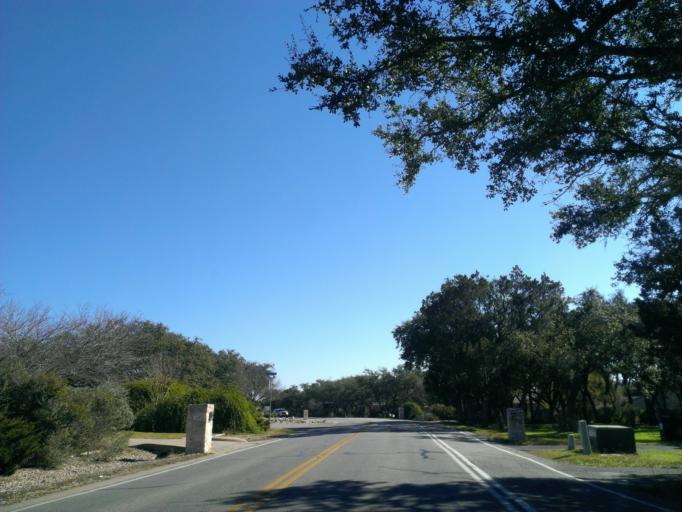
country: US
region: Texas
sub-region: Travis County
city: Lakeway
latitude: 30.3706
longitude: -97.9767
